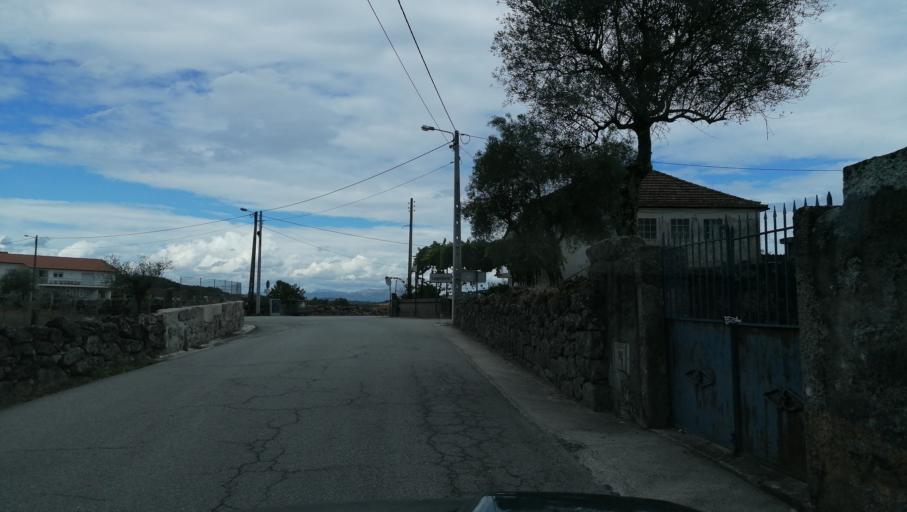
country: PT
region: Vila Real
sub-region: Vila Pouca de Aguiar
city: Vila Pouca de Aguiar
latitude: 41.5461
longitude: -7.6157
